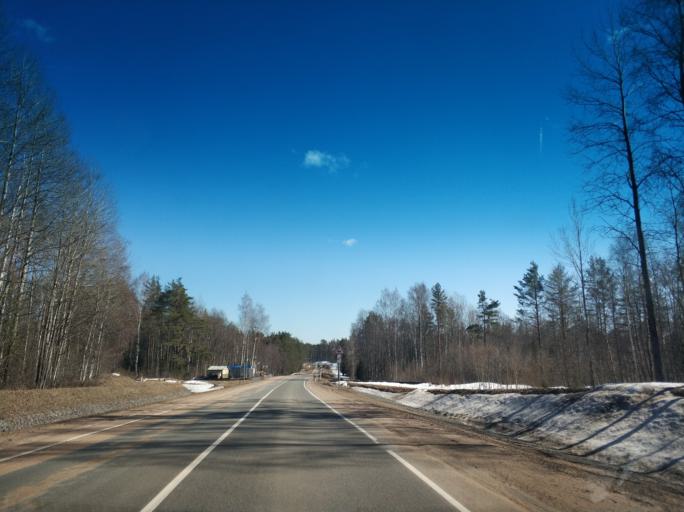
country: RU
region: Leningrad
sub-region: Vsevolzhskij Rajon
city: Vaskelovo
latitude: 60.4259
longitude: 30.2489
